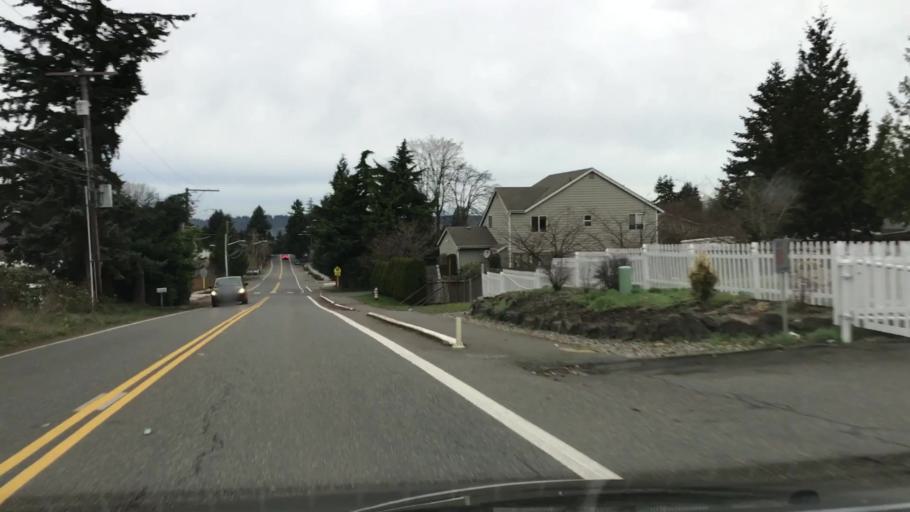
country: US
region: Washington
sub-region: King County
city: East Hill-Meridian
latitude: 47.4088
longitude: -122.2018
